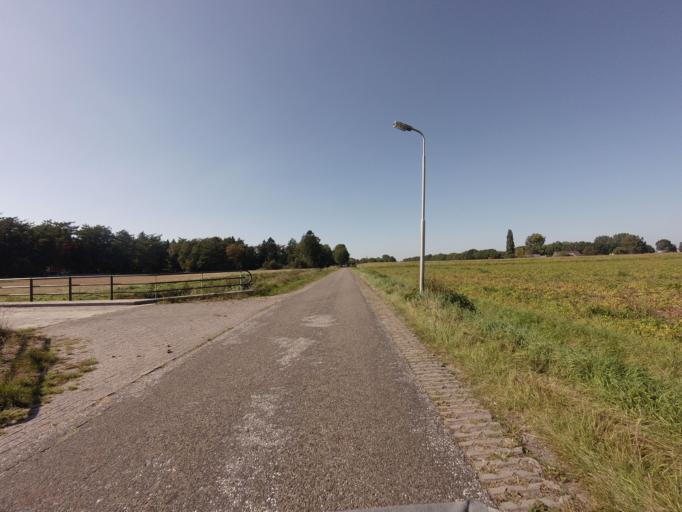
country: NL
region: Overijssel
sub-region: Gemeente Hardenberg
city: Hardenberg
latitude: 52.5316
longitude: 6.6404
